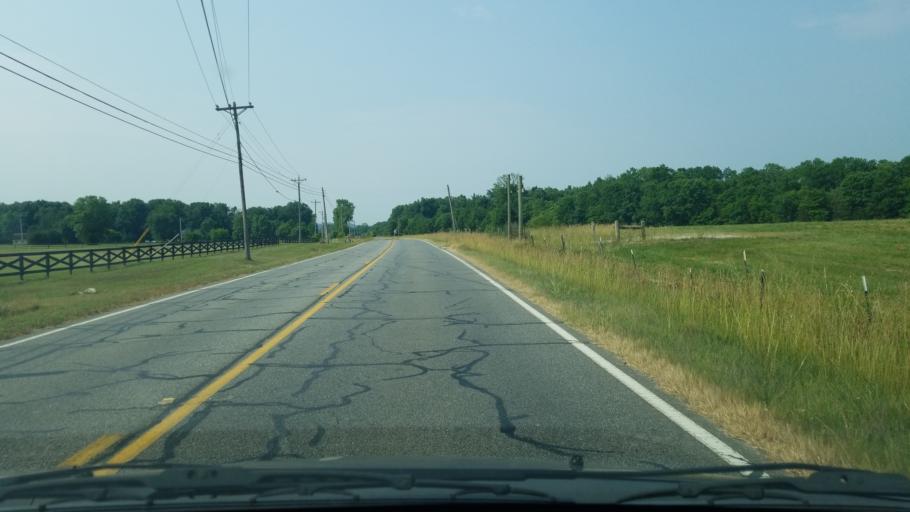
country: US
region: Georgia
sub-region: Catoosa County
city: Ringgold
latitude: 34.9632
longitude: -85.1029
